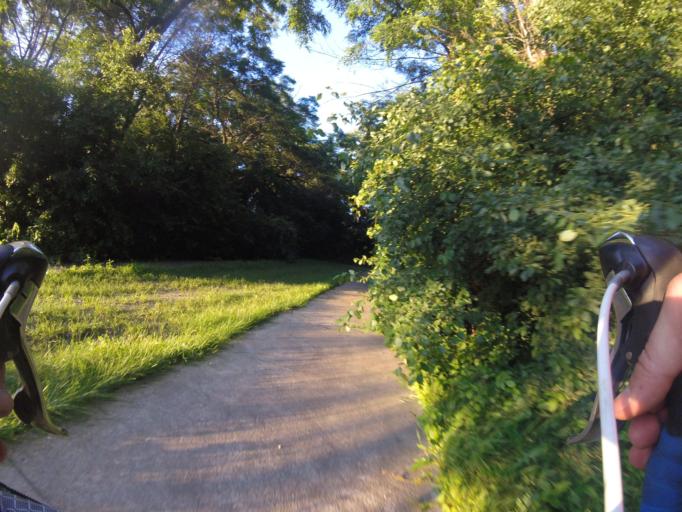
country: CA
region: Ontario
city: Bells Corners
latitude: 45.3495
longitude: -75.8471
